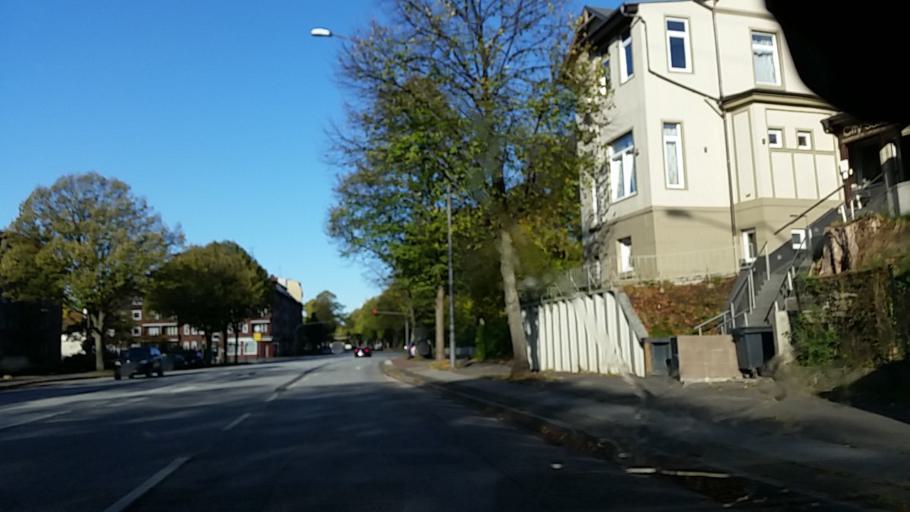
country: DE
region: Hamburg
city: Marienthal
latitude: 53.5453
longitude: 10.0890
